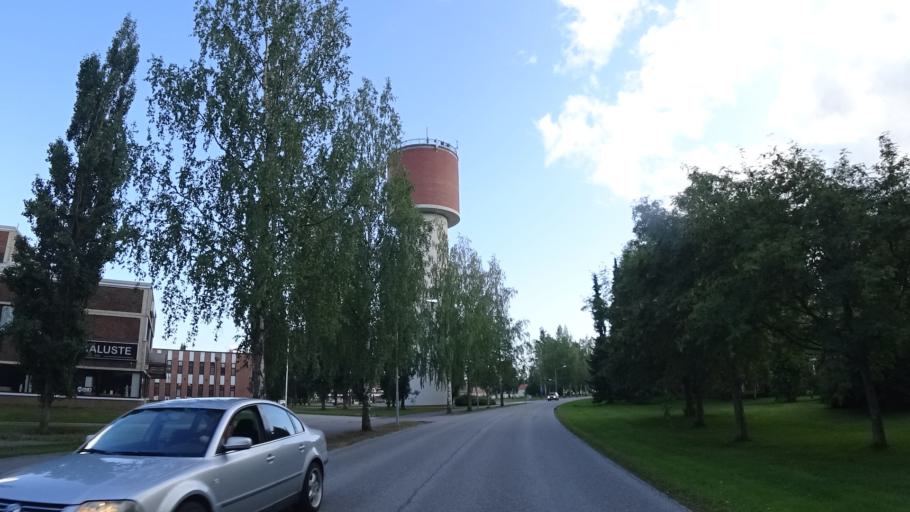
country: FI
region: North Karelia
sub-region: Pielisen Karjala
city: Lieksa
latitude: 63.3226
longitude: 30.0227
